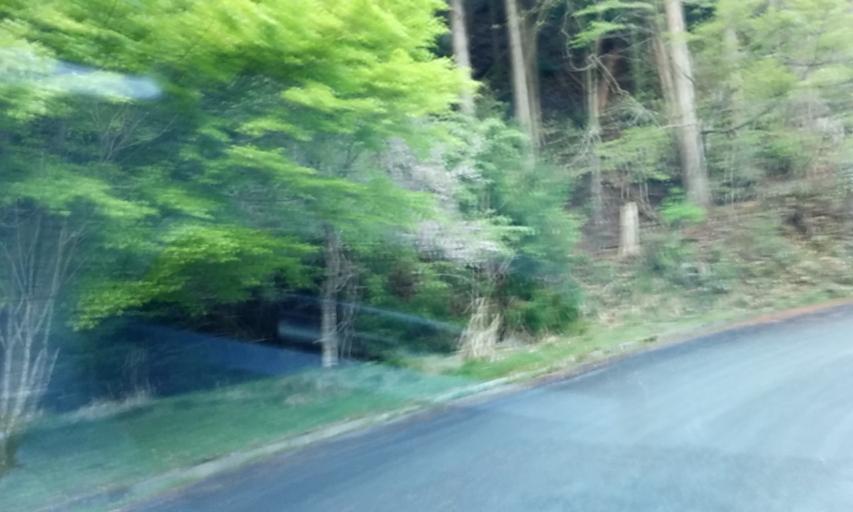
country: JP
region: Kyoto
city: Ayabe
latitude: 35.2576
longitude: 135.3234
